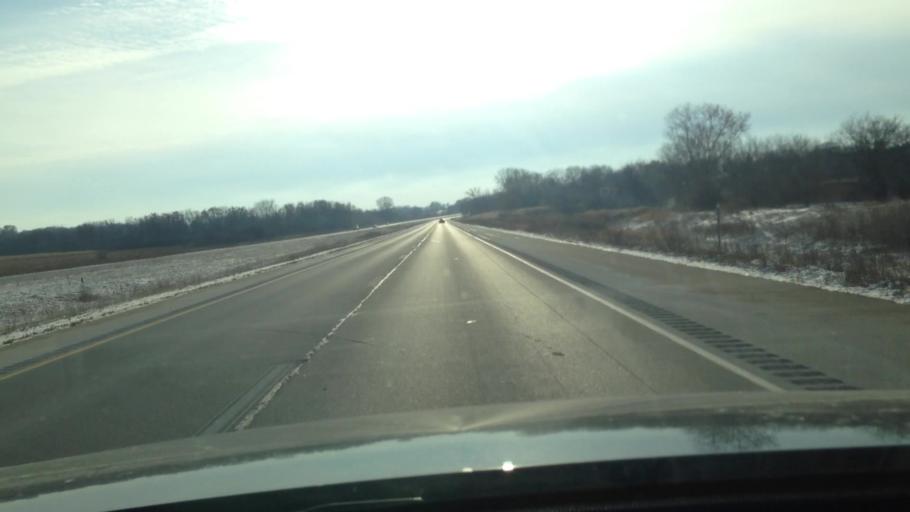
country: US
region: Wisconsin
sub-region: Walworth County
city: Potter Lake
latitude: 42.8147
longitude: -88.3644
